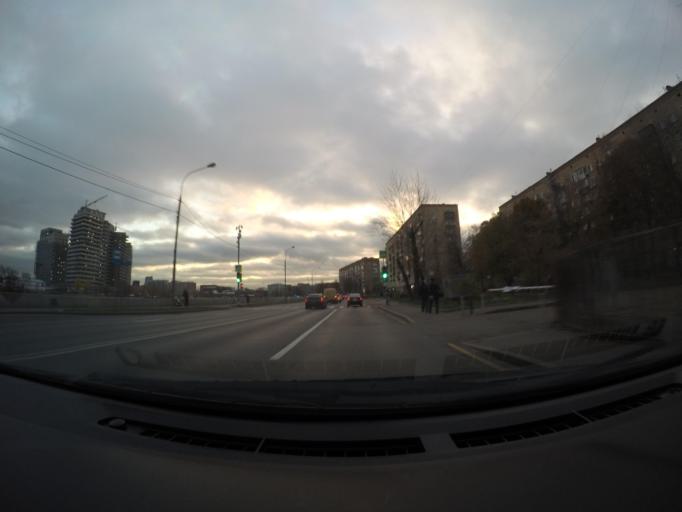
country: RU
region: Moscow
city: Taganskiy
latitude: 55.7200
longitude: 37.6517
